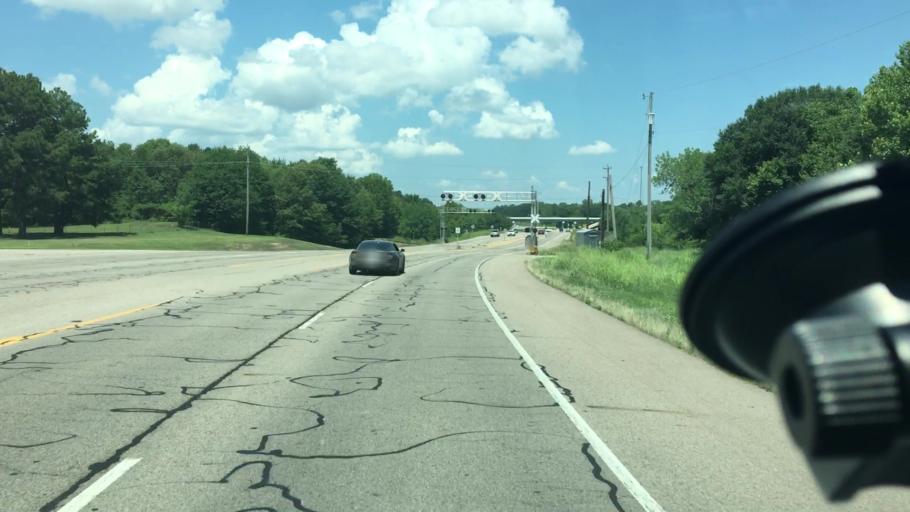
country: US
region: Arkansas
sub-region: Sebastian County
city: Barling
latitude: 35.3185
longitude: -94.2867
